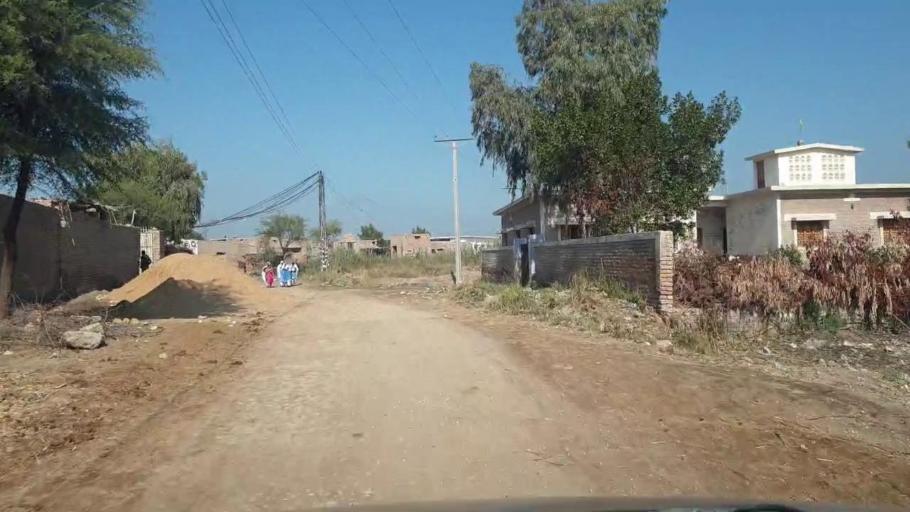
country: PK
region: Sindh
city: Bhit Shah
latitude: 25.8856
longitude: 68.5267
